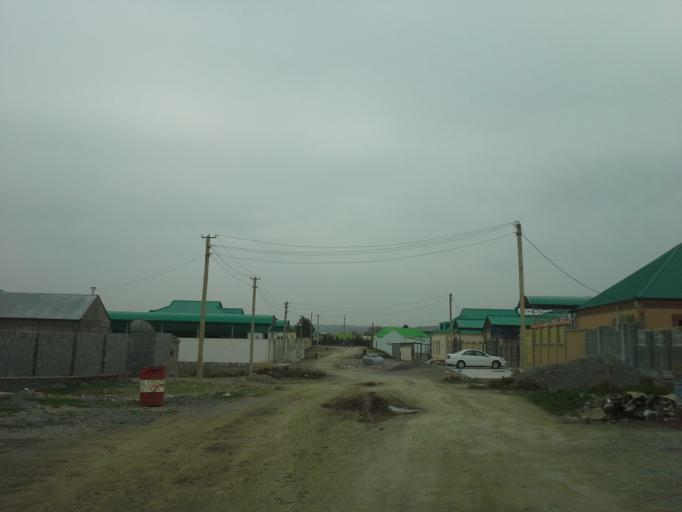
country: TM
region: Ahal
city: Abadan
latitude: 37.9771
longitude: 58.2240
